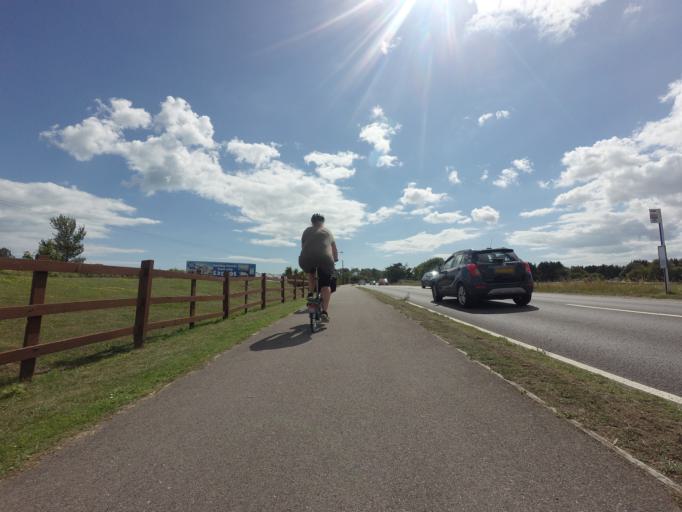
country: GB
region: England
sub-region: East Sussex
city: Pevensey
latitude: 50.8071
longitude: 0.3395
